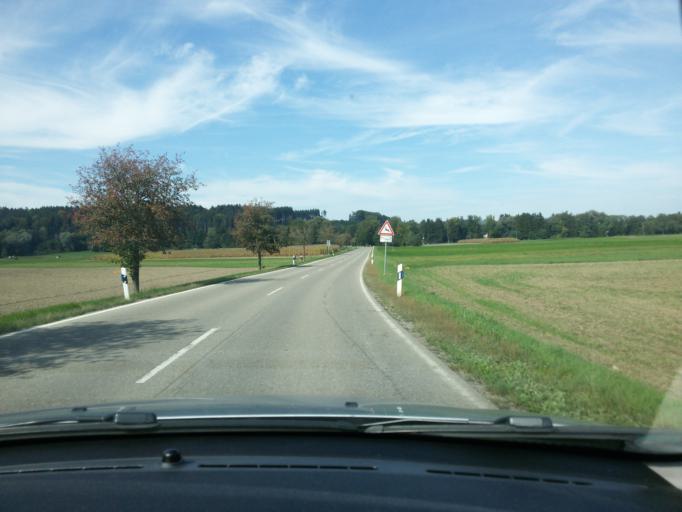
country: DE
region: Bavaria
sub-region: Swabia
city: Wehringen
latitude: 48.2560
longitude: 10.7875
